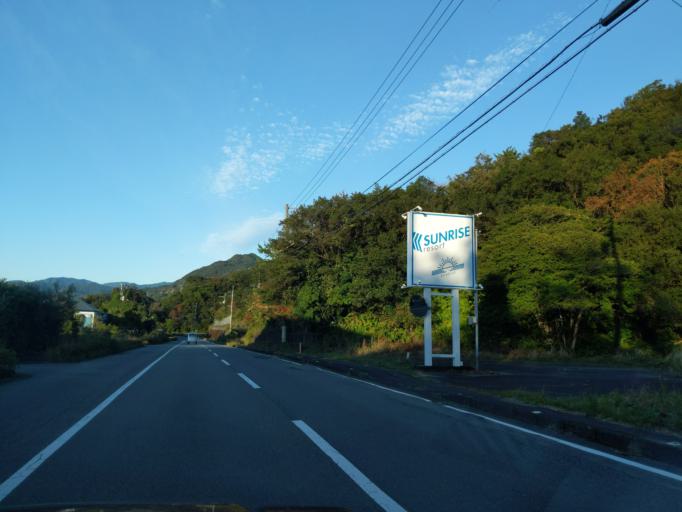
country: JP
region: Kochi
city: Muroto-misakicho
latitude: 33.5857
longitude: 134.3361
